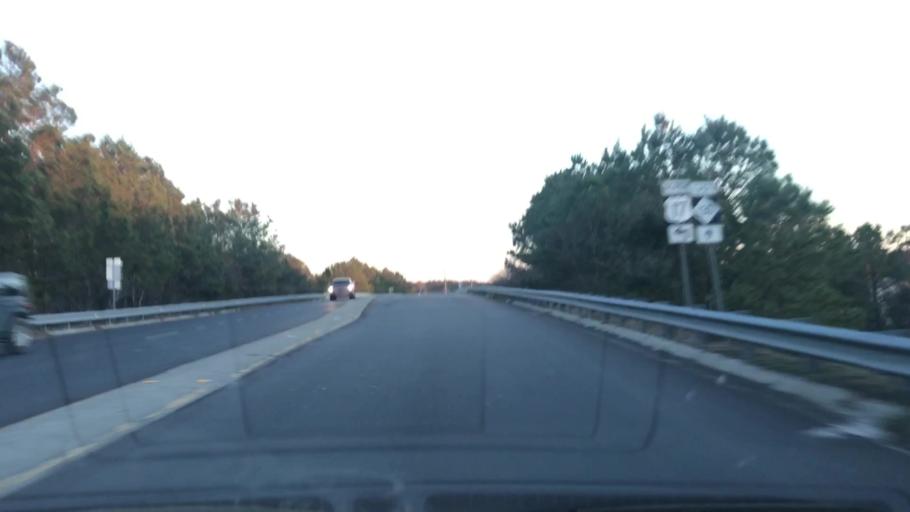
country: US
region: North Carolina
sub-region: Brunswick County
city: Shallotte
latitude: 33.9768
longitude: -78.4060
